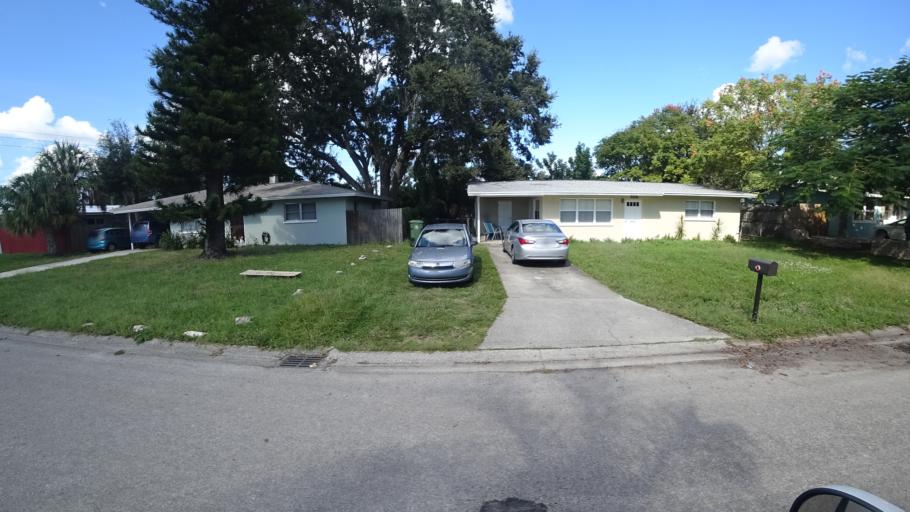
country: US
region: Florida
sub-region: Manatee County
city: South Bradenton
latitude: 27.4777
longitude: -82.5872
